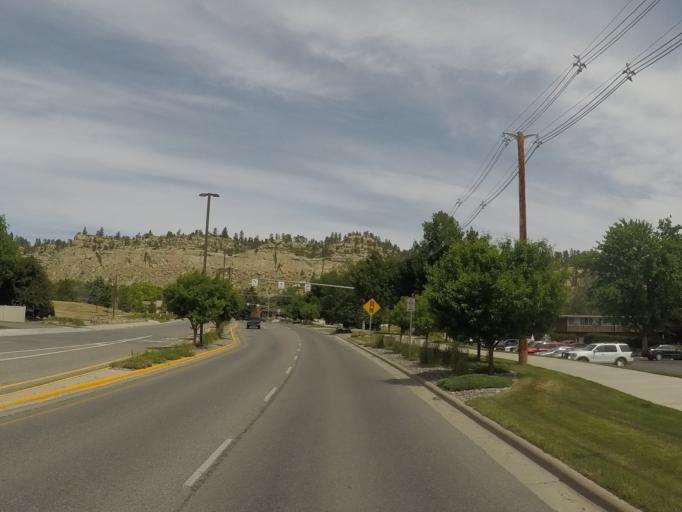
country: US
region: Montana
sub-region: Yellowstone County
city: Billings
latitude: 45.7968
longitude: -108.6174
